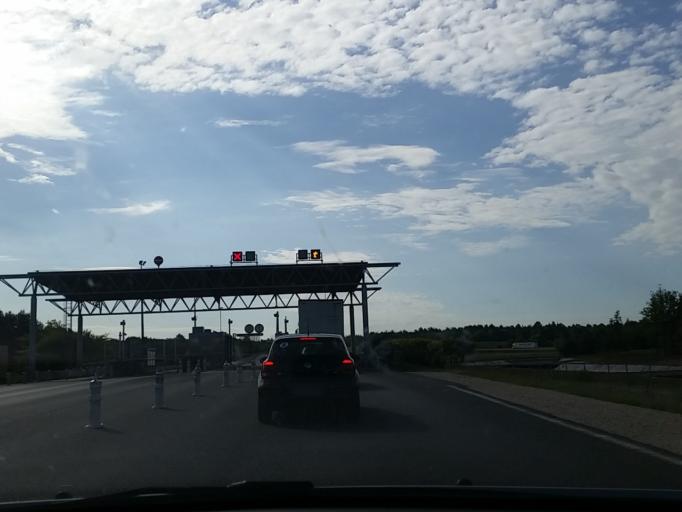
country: FR
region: Centre
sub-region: Departement du Loir-et-Cher
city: Villefranche-sur-Cher
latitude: 47.3250
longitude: 1.7650
